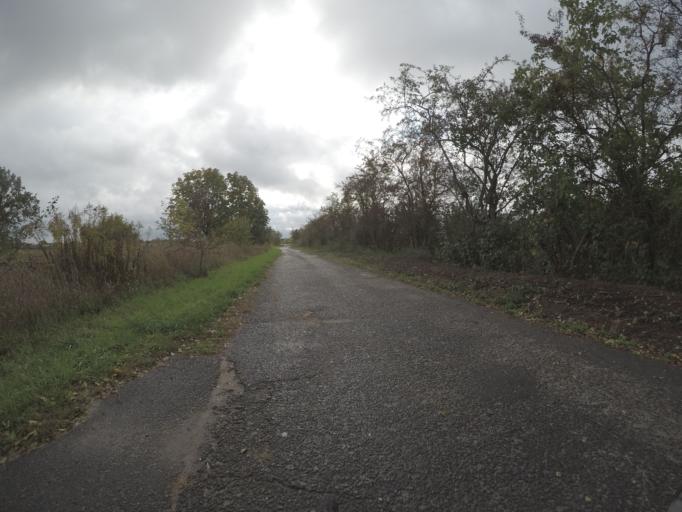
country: DE
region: Berlin
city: Blankenfelde
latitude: 52.6635
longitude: 13.3887
